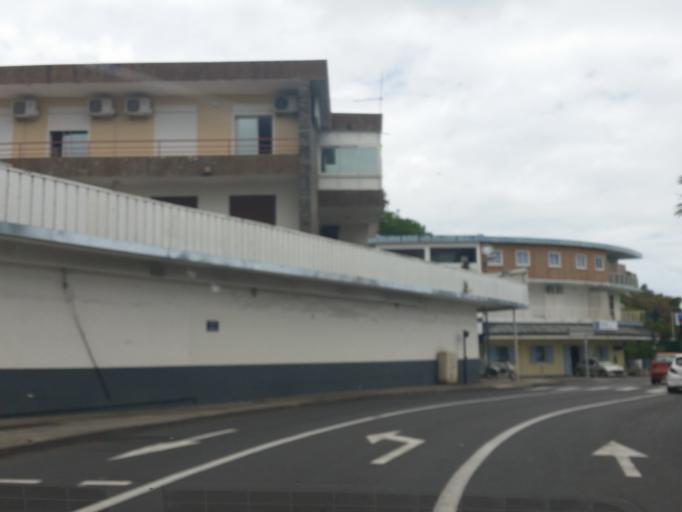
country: RE
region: Reunion
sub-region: Reunion
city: Saint-Denis
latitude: -20.8962
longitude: 55.4580
